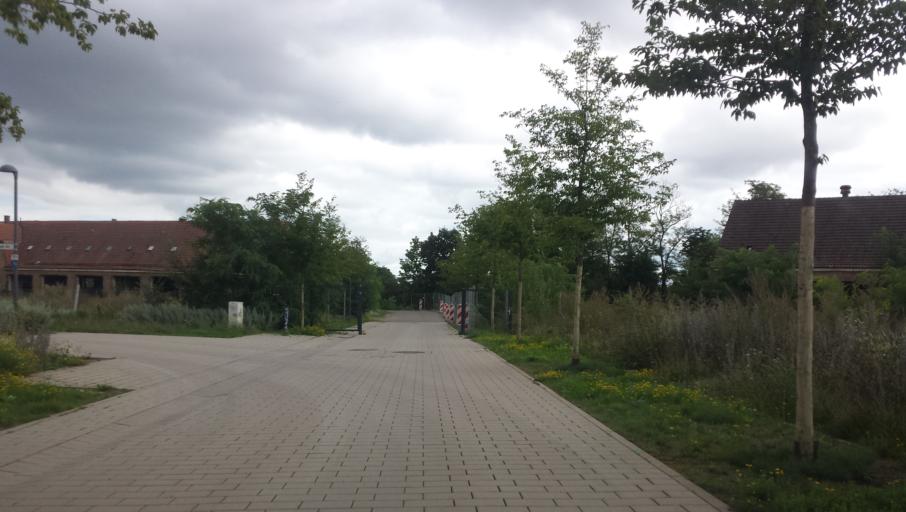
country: DE
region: Rheinland-Pfalz
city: Landau in der Pfalz
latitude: 49.1886
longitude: 8.1234
